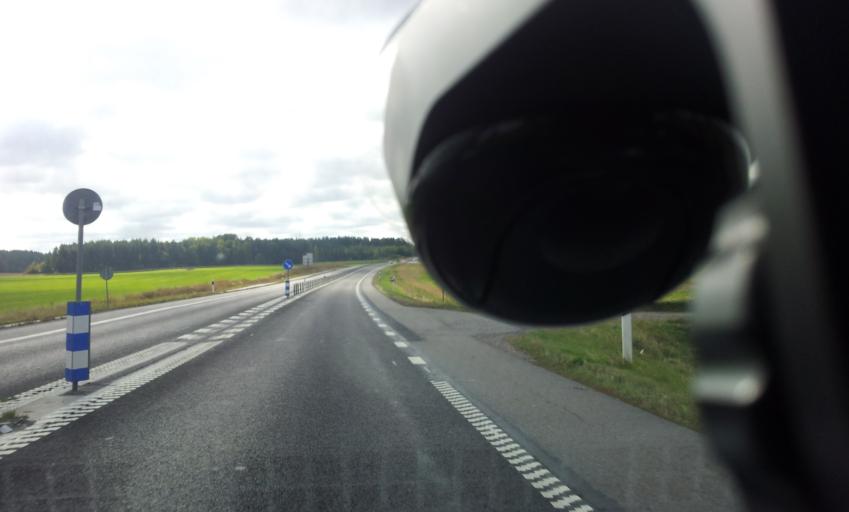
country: SE
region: OEstergoetland
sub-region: Soderkopings Kommun
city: Soederkoeping
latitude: 58.5286
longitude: 16.2869
